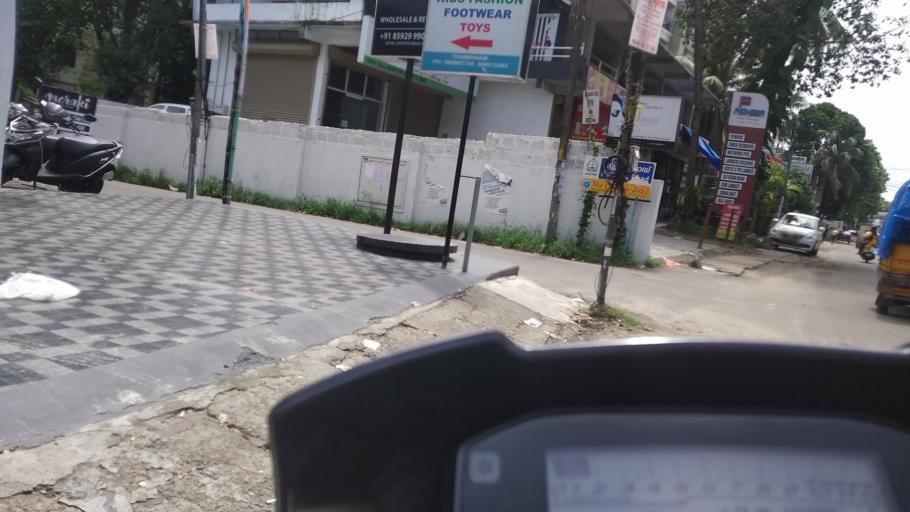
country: IN
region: Kerala
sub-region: Ernakulam
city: Cochin
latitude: 9.9888
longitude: 76.3101
